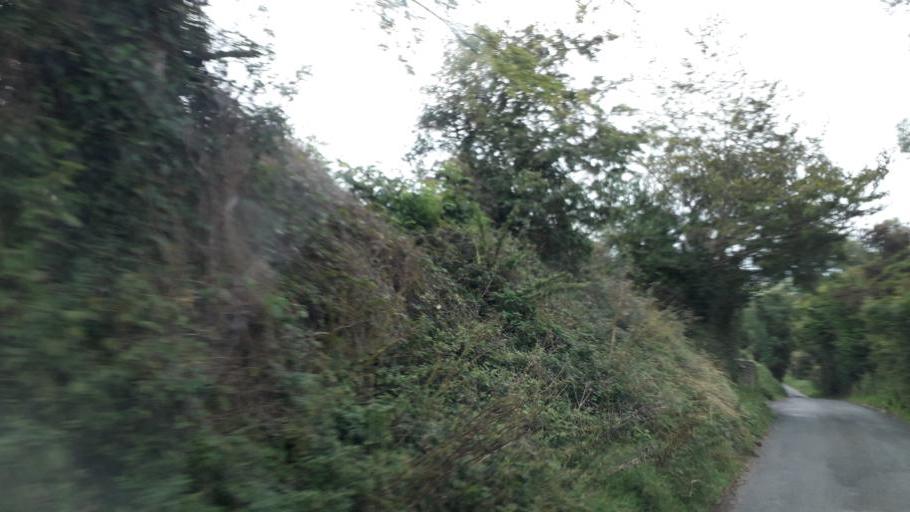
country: IE
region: Leinster
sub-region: Wicklow
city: Enniskerry
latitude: 53.1812
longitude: -6.2077
